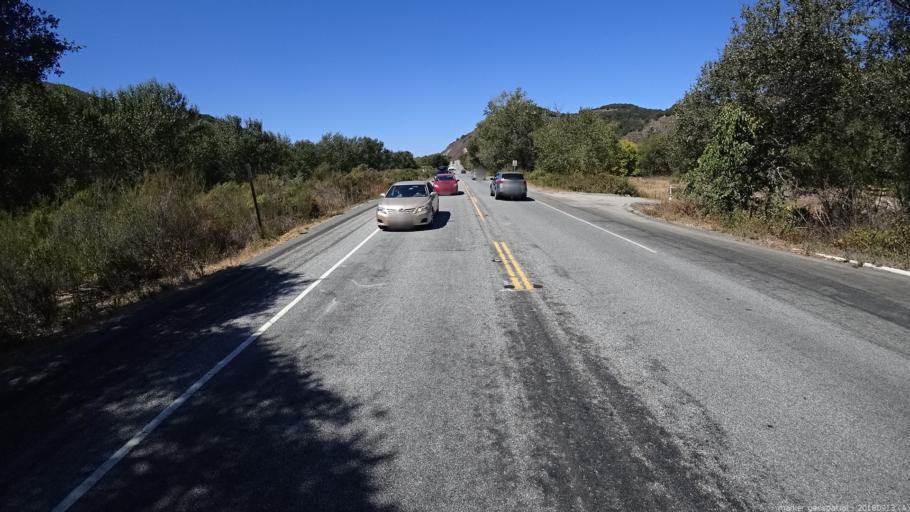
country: US
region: California
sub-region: Monterey County
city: Carmel Valley Village
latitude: 36.5112
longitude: -121.7700
